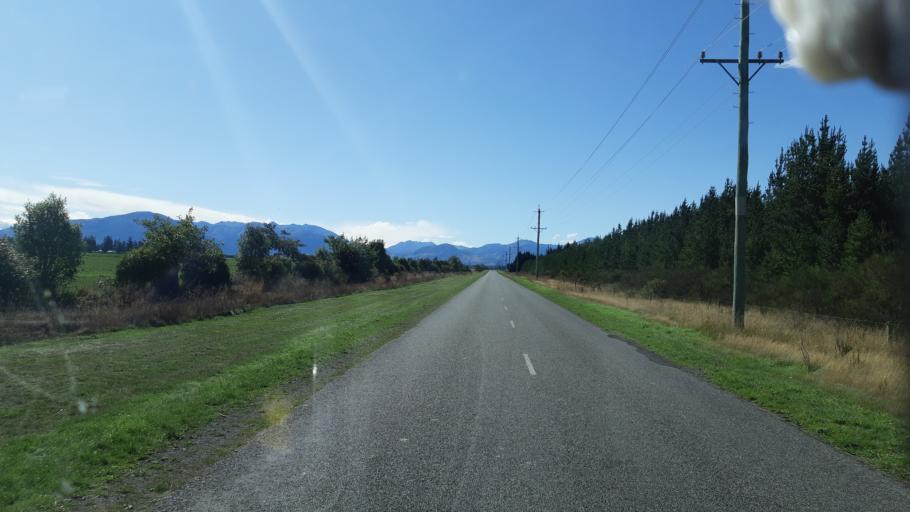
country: NZ
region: Canterbury
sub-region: Ashburton District
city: Methven
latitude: -43.7844
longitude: 171.5357
